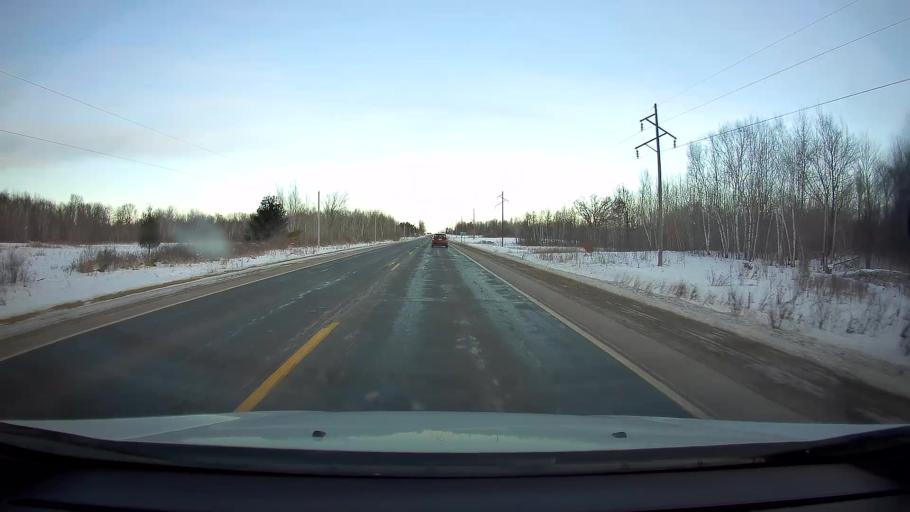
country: US
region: Wisconsin
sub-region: Barron County
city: Turtle Lake
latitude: 45.3564
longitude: -92.1669
